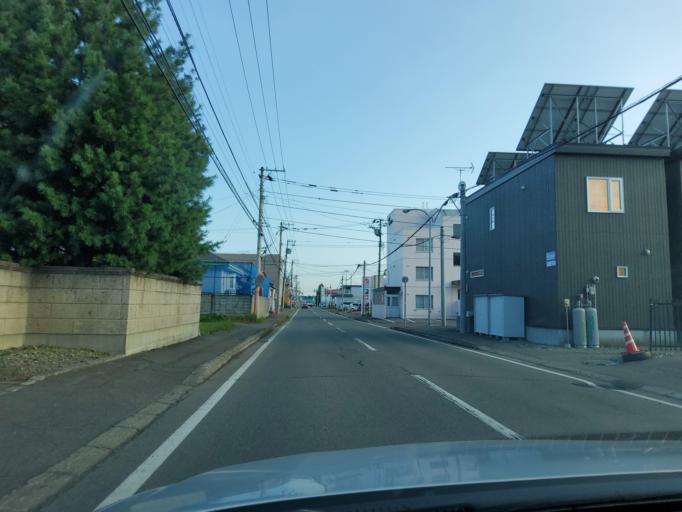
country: JP
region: Hokkaido
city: Obihiro
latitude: 42.9323
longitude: 143.1835
